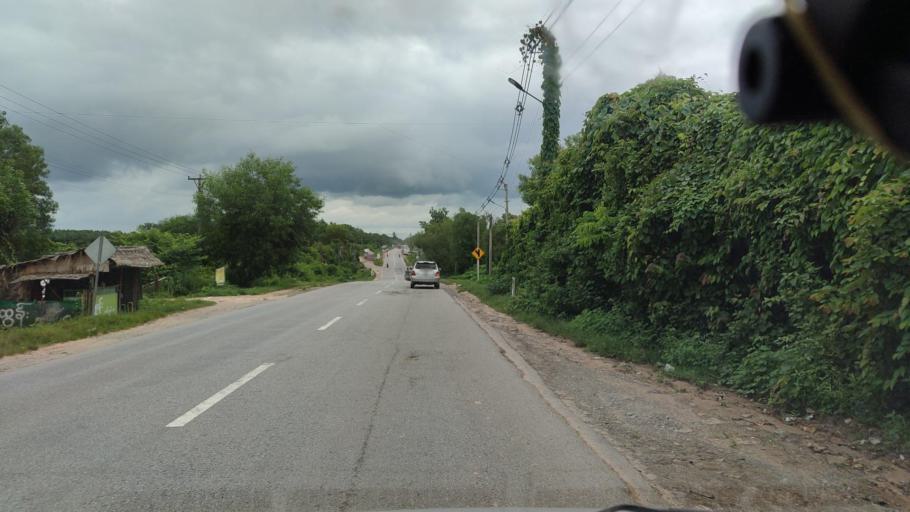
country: MM
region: Bago
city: Bago
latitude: 17.3478
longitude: 96.4484
